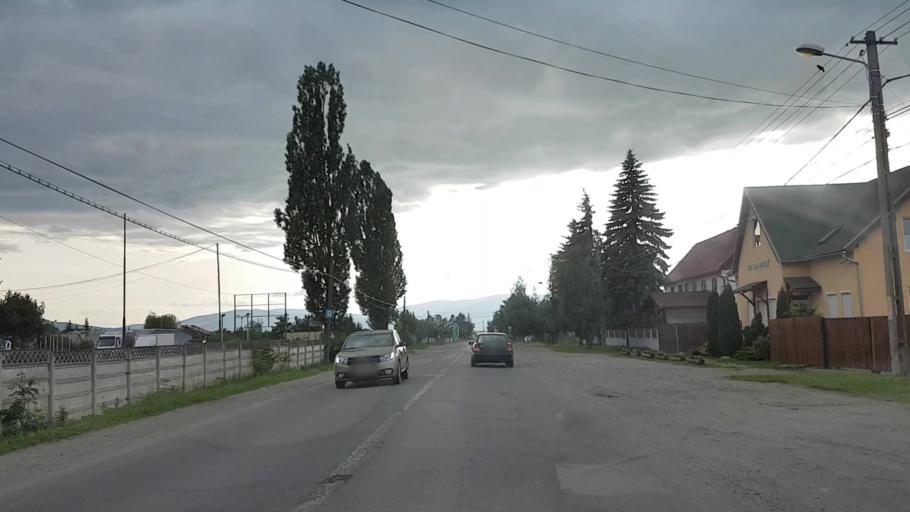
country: RO
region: Harghita
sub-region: Municipiul Gheorgheni
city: Gheorgheni
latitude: 46.7137
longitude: 25.5713
